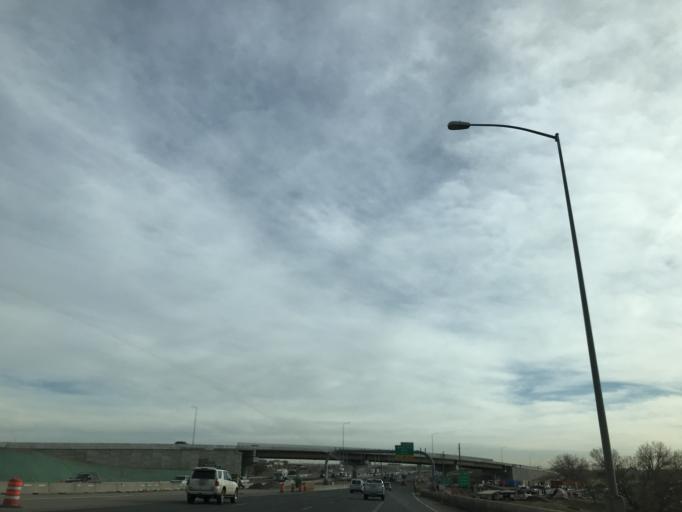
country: US
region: Colorado
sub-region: Adams County
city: Commerce City
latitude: 39.7782
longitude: -104.8998
